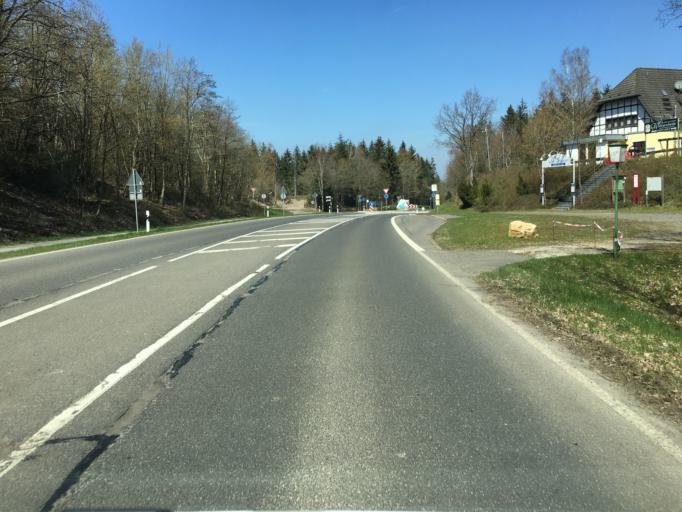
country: DE
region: Rheinland-Pfalz
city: Hummel
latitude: 50.4999
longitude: 6.8199
